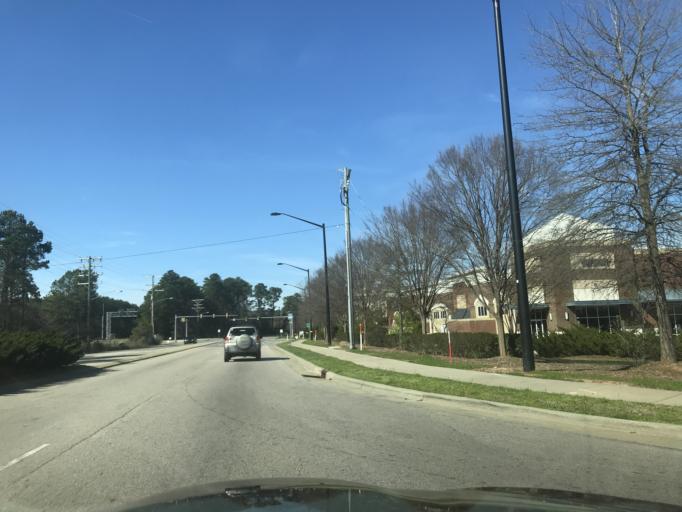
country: US
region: North Carolina
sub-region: Wake County
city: Morrisville
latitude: 35.8670
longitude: -78.8493
